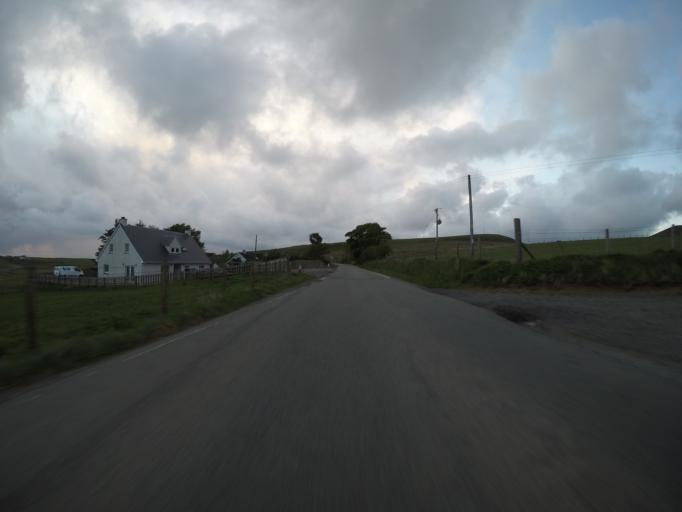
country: GB
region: Scotland
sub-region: Highland
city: Portree
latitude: 57.6203
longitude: -6.3736
